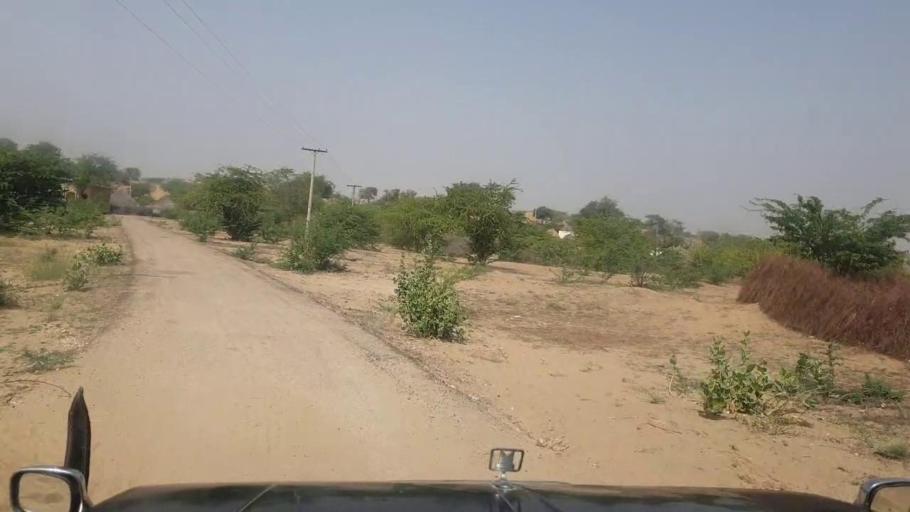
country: PK
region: Sindh
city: Islamkot
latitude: 25.0993
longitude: 70.1769
